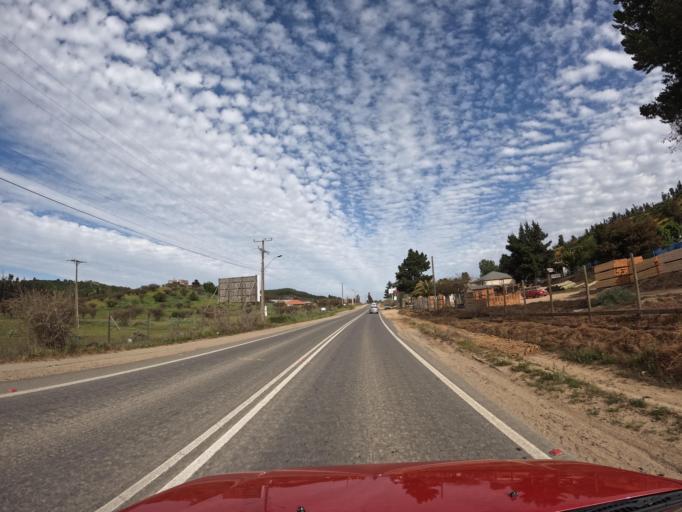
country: CL
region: O'Higgins
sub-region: Provincia de Colchagua
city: Santa Cruz
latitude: -34.3040
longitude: -71.7854
